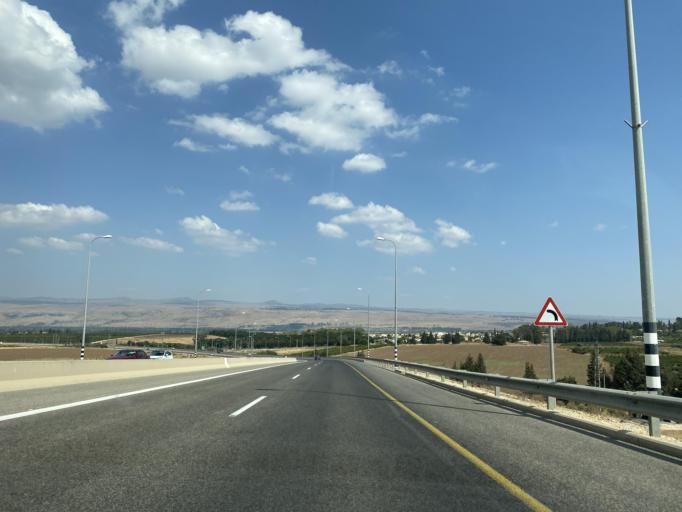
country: IL
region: Northern District
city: Rosh Pinna
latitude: 33.0281
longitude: 35.5641
